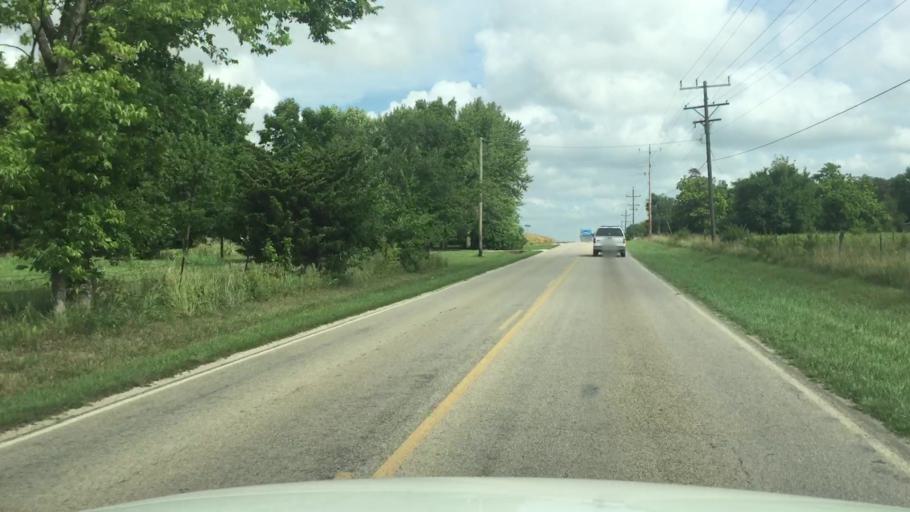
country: US
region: Kansas
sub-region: Allen County
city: Humboldt
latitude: 37.8373
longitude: -95.4368
